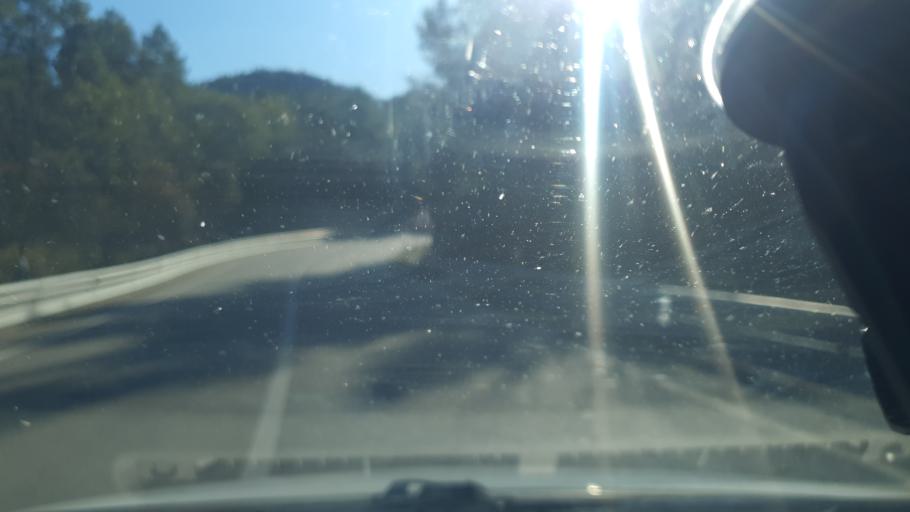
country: ES
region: Castille and Leon
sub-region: Provincia de Avila
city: Arenas de San Pedro
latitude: 40.2098
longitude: -5.0413
